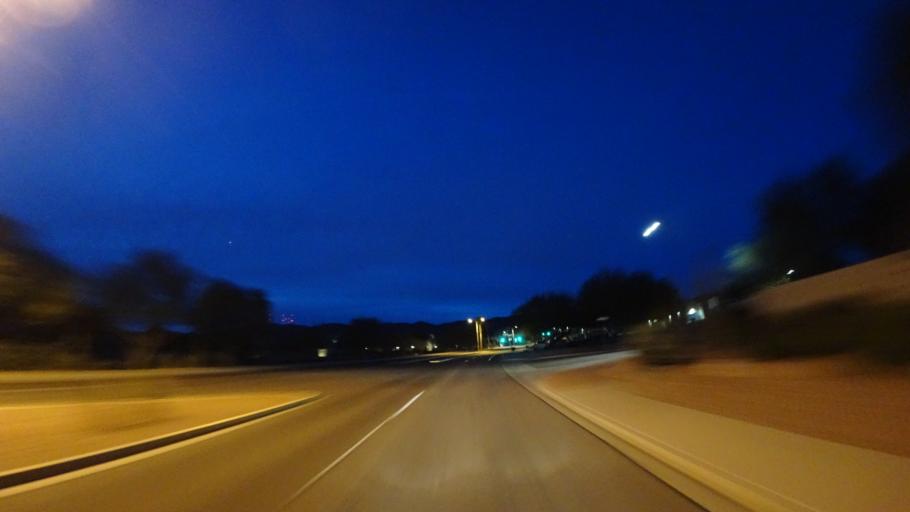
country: US
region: Arizona
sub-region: Maricopa County
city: Guadalupe
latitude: 33.3070
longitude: -112.0271
